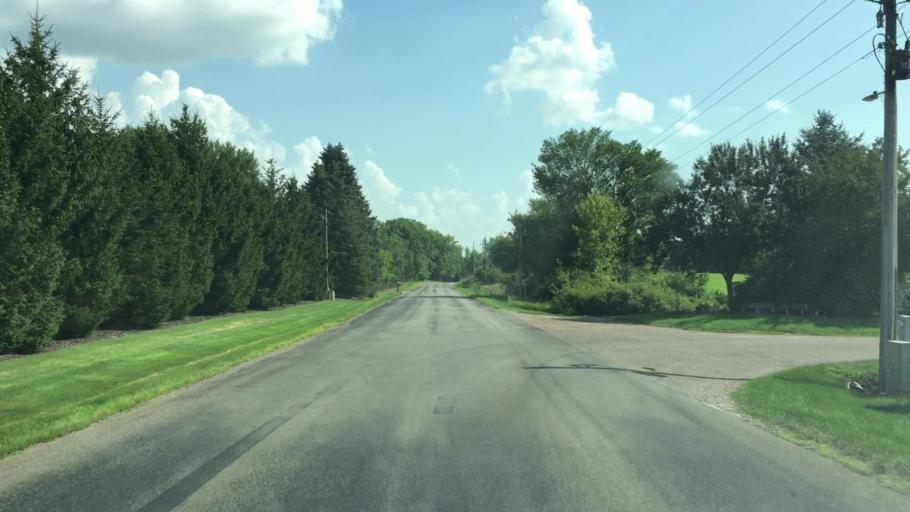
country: US
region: Iowa
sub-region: Johnson County
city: North Liberty
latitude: 41.8079
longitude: -91.6155
